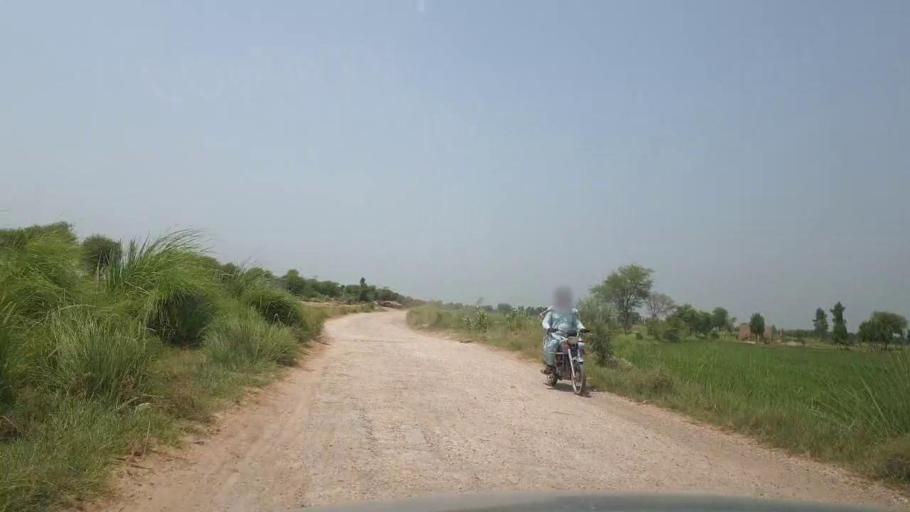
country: PK
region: Sindh
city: Garhi Yasin
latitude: 27.8833
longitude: 68.4407
